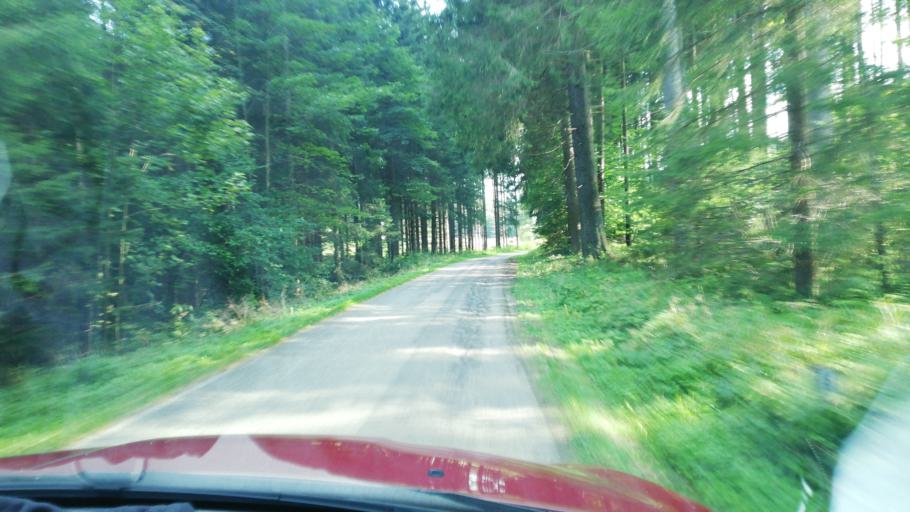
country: AT
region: Lower Austria
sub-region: Politischer Bezirk Zwettl
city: Langschlag
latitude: 48.4762
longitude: 14.8401
